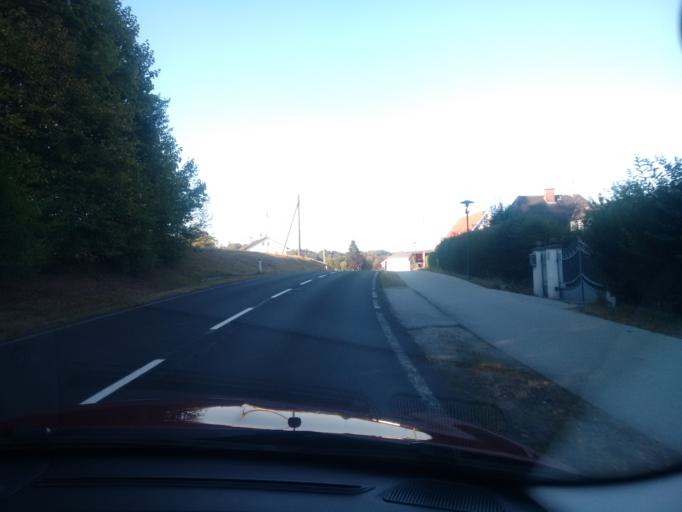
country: DE
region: Bavaria
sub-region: Upper Bavaria
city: Burghausen
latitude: 48.1598
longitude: 12.8418
